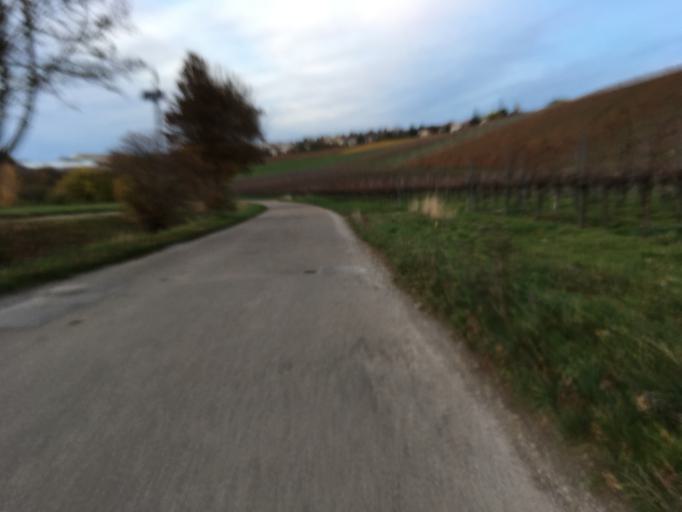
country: DE
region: Baden-Wuerttemberg
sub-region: Regierungsbezirk Stuttgart
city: Neckarwestheim
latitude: 49.0395
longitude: 9.1890
